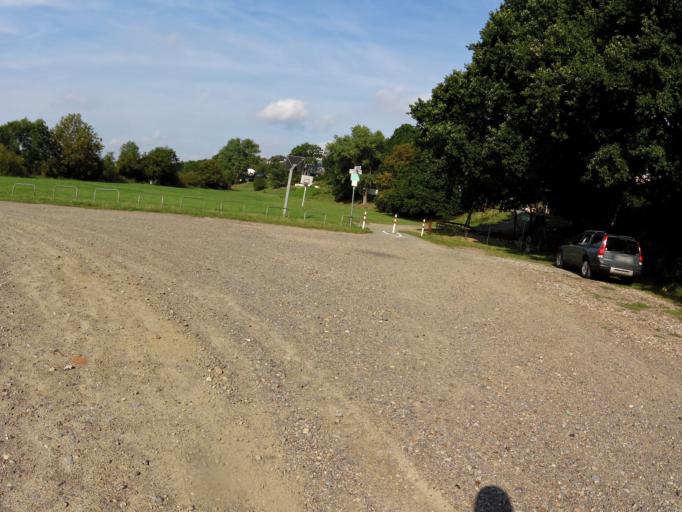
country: DE
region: Lower Saxony
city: Ahsen-Oetzen
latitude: 52.9964
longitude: 9.0795
